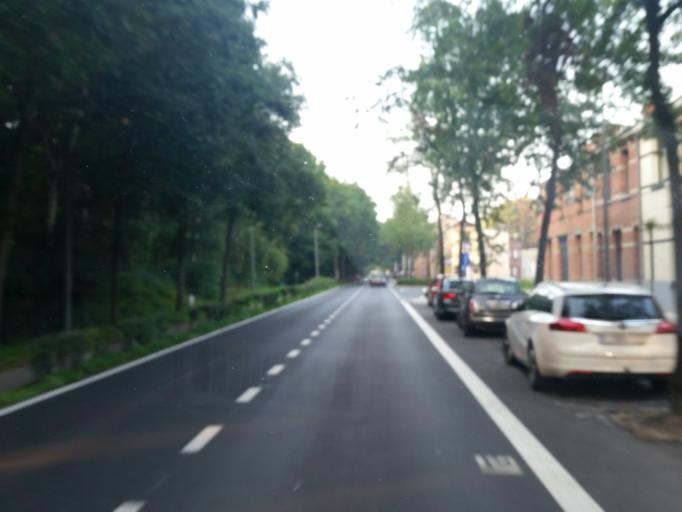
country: BE
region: Flanders
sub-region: Provincie Antwerpen
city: Brasschaat
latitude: 51.2974
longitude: 4.4985
